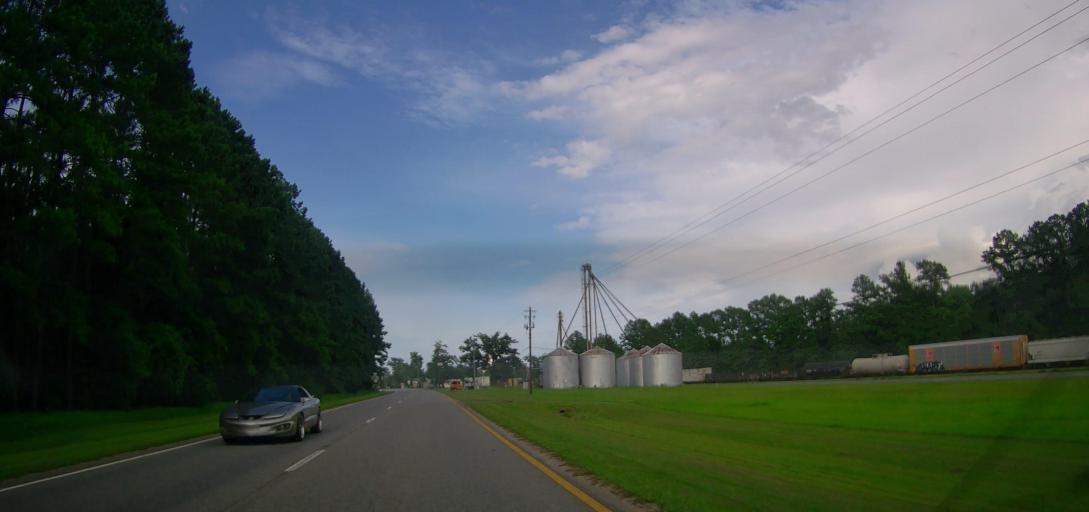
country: US
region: Georgia
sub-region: Wayne County
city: Jesup
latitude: 31.4813
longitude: -82.0231
